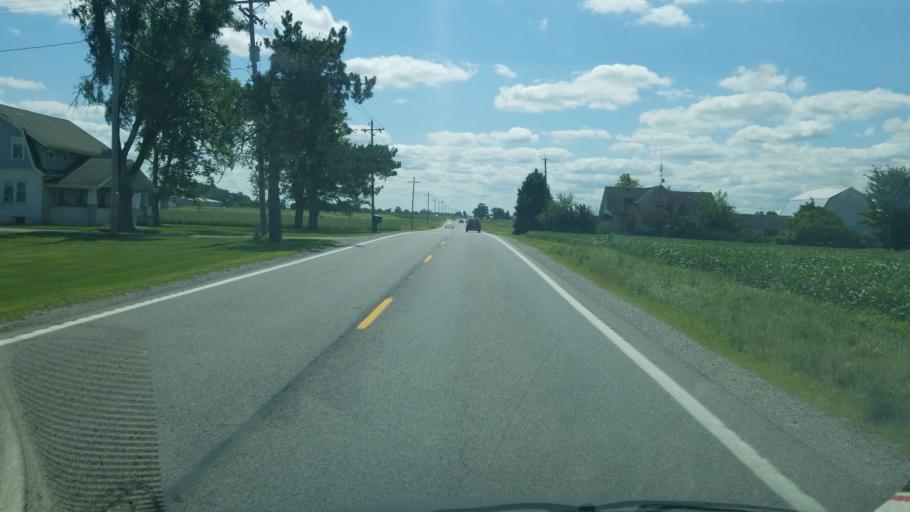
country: US
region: Ohio
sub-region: Fulton County
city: Delta
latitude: 41.6531
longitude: -84.0353
